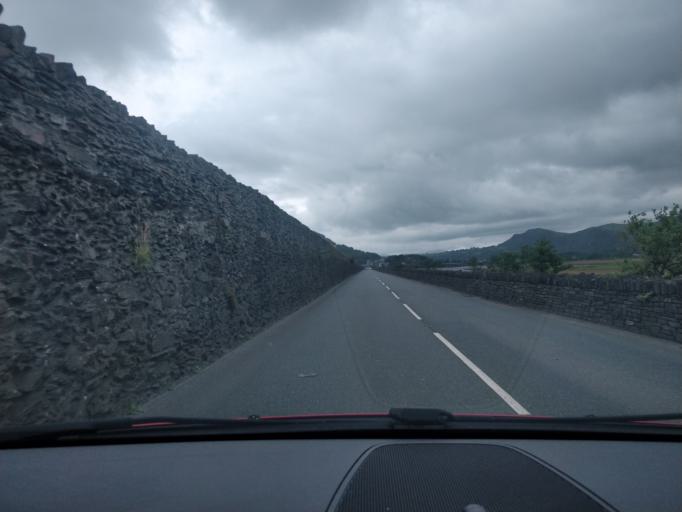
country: GB
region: Wales
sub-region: Gwynedd
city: Porthmadog
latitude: 52.9205
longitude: -4.1116
